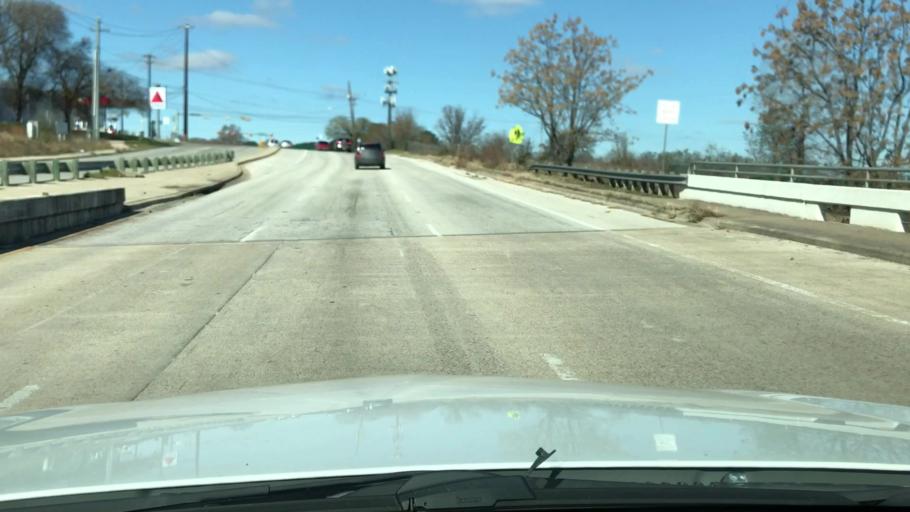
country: US
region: Texas
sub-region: Travis County
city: Onion Creek
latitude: 30.1785
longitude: -97.7455
